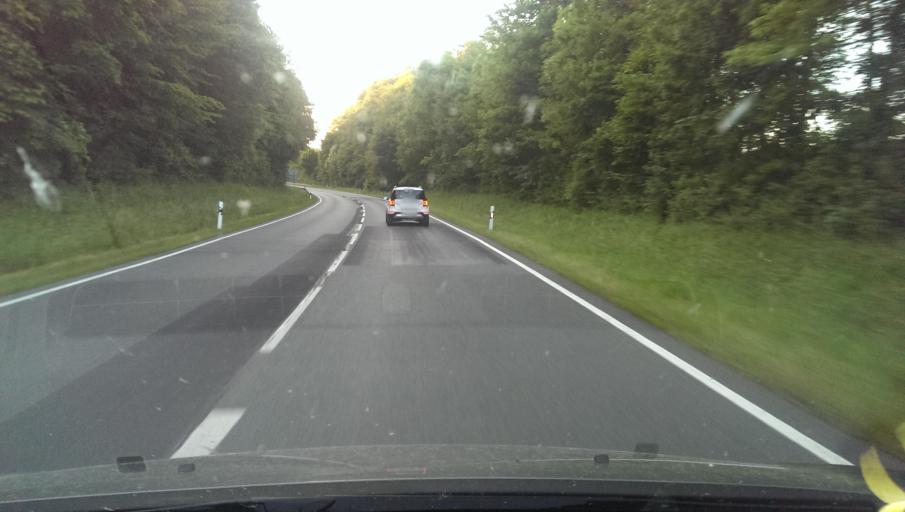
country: DE
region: Bavaria
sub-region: Regierungsbezirk Unterfranken
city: Wuerzburg
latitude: 49.7664
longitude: 9.8585
